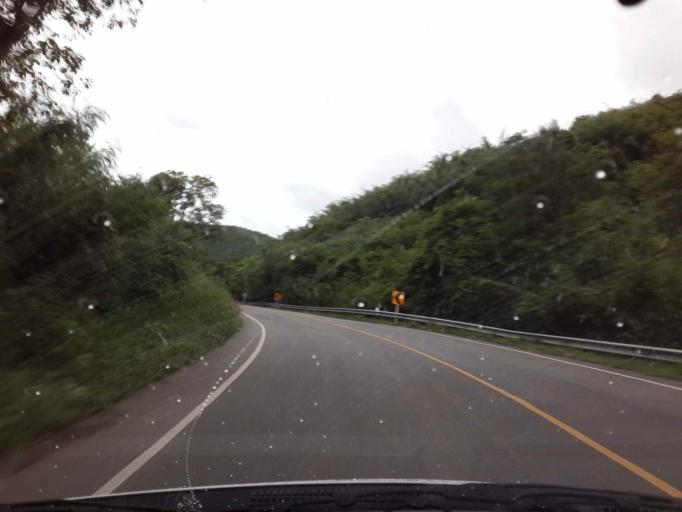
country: TH
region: Ratchaburi
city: Suan Phueng
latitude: 13.5801
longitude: 99.2511
